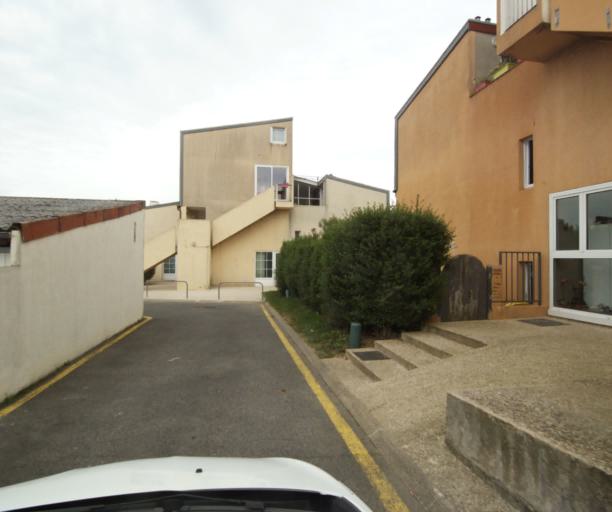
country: FR
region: Ile-de-France
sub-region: Departement de Seine-et-Marne
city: Torcy
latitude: 48.8521
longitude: 2.6551
